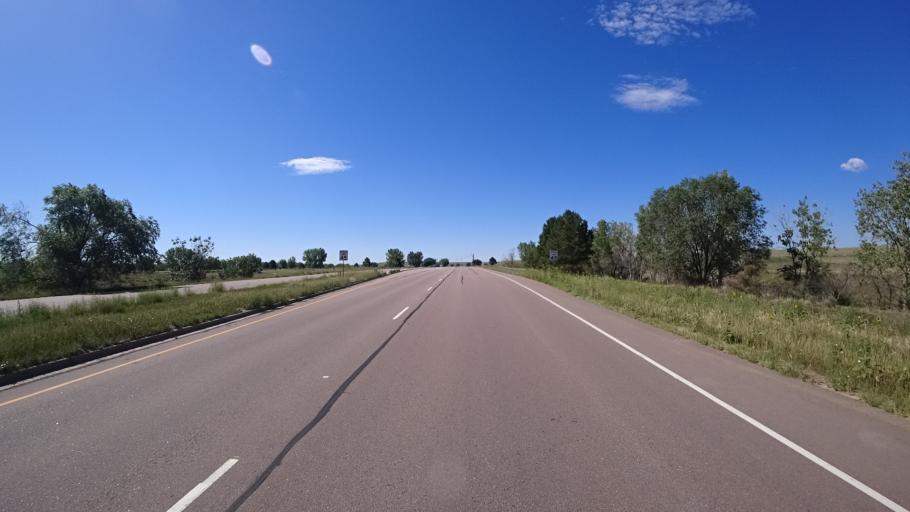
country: US
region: Colorado
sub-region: El Paso County
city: Security-Widefield
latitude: 38.7647
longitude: -104.6597
